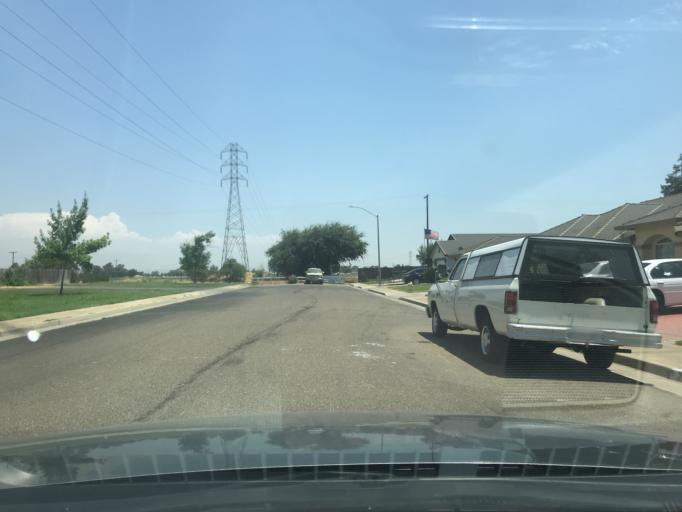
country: US
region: California
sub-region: Merced County
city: Atwater
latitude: 37.3675
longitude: -120.5918
